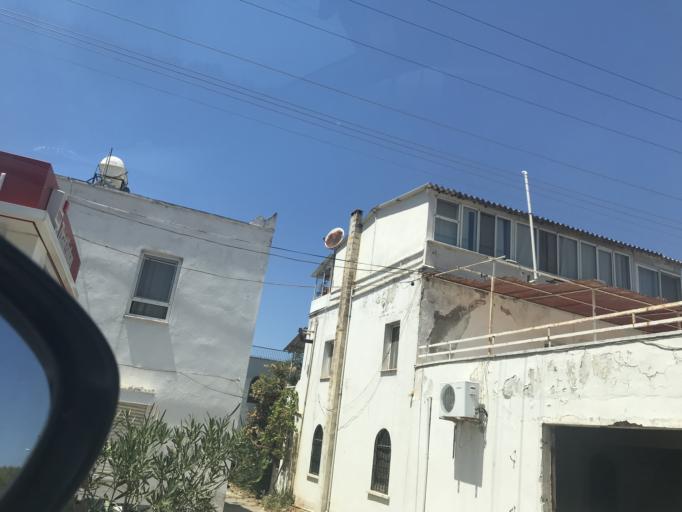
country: TR
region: Mugla
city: Karaova
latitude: 37.1365
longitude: 27.5825
